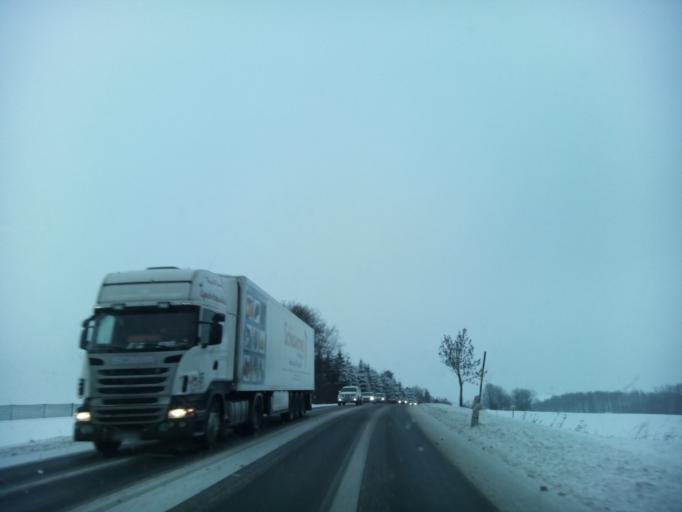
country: DE
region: Saxony
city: Grossolbersdorf
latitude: 50.7111
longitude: 13.1018
